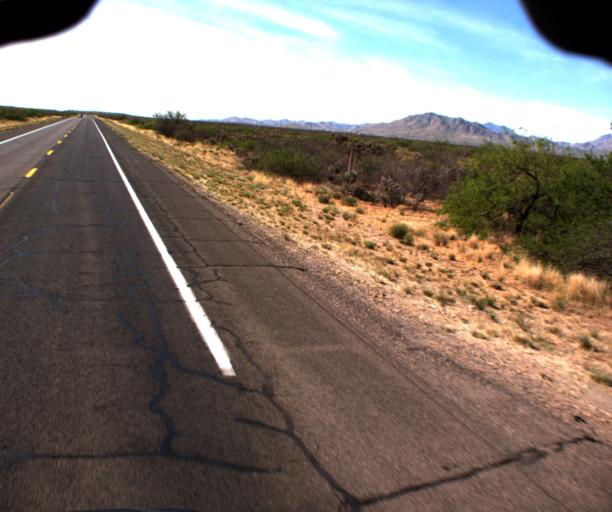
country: US
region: Arizona
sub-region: Graham County
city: Swift Trail Junction
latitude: 32.6552
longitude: -109.6993
